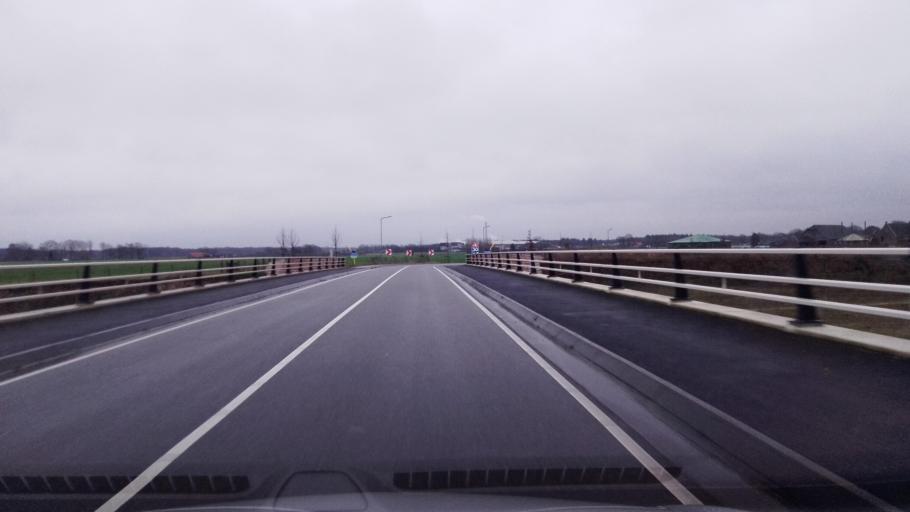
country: NL
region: Limburg
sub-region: Gemeente Bergen
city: Wellerlooi
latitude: 51.5259
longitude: 6.1138
